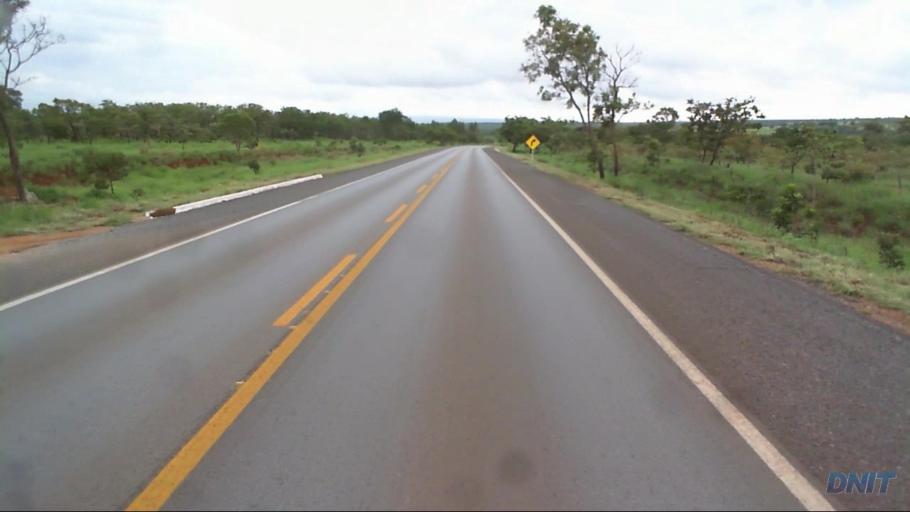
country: BR
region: Goias
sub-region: Barro Alto
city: Barro Alto
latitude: -15.2093
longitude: -48.6745
